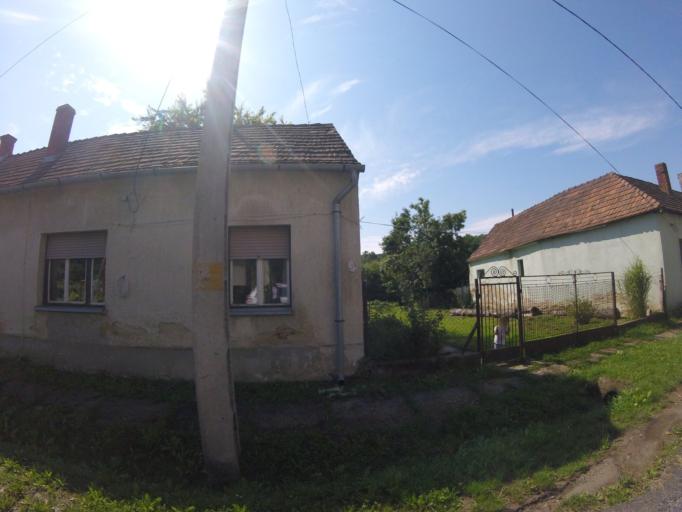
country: HU
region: Zala
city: Letenye
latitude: 46.5404
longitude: 16.6938
